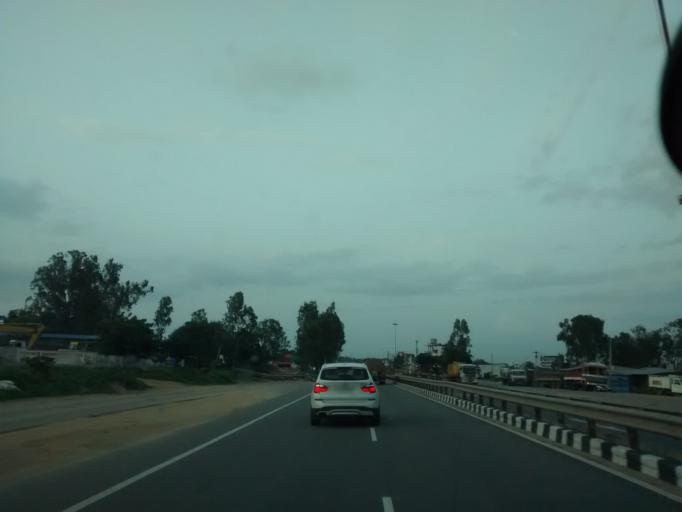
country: IN
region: Telangana
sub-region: Mahbubnagar
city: Mahbubnagar
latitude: 16.7689
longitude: 78.1265
